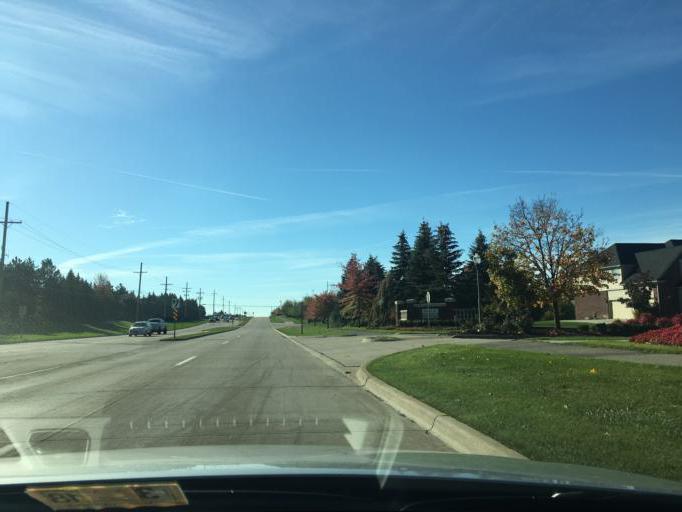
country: US
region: Michigan
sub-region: Wayne County
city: Northville
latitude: 42.4048
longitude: -83.5109
